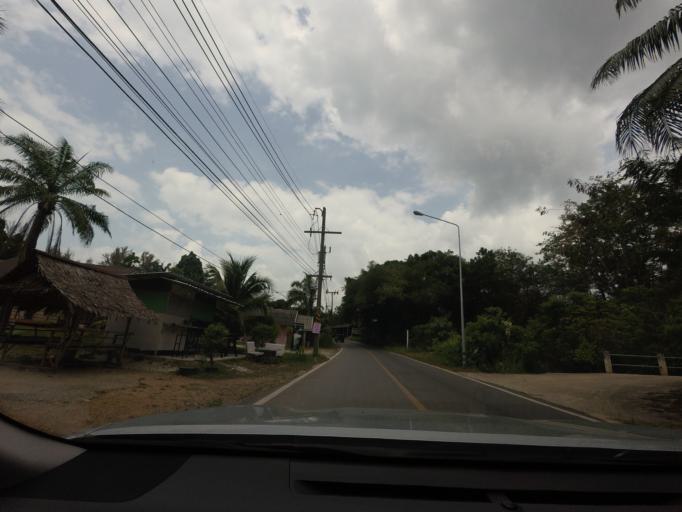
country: TH
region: Phangnga
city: Ban Ao Nang
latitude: 8.0825
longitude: 98.7456
